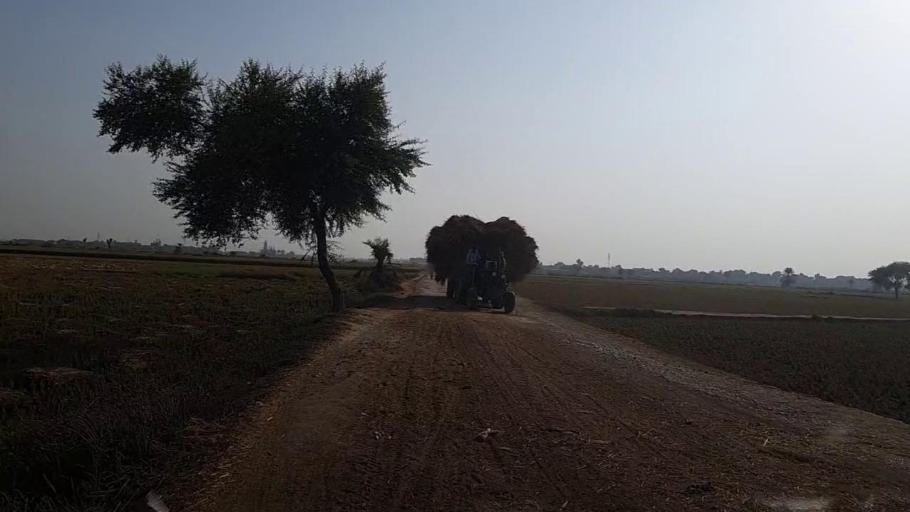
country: PK
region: Sindh
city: Kandhkot
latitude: 28.2839
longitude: 69.2568
